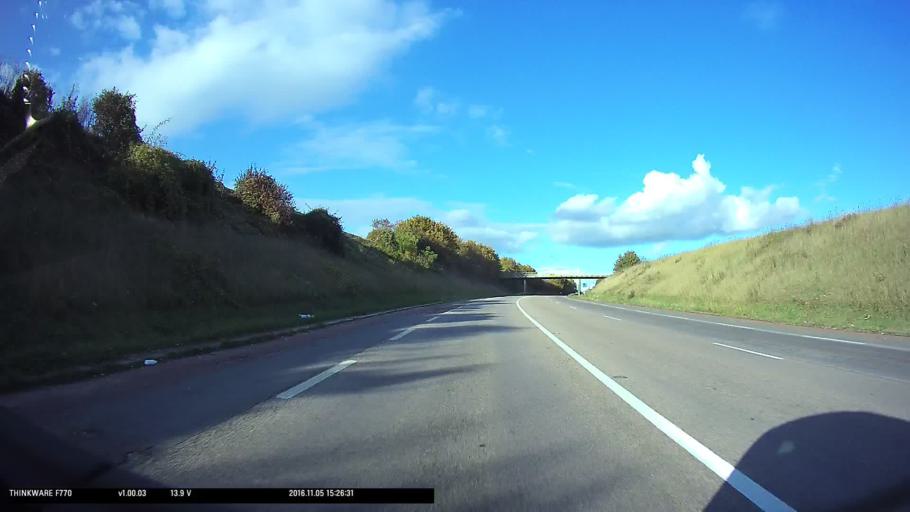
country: FR
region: Ile-de-France
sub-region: Departement des Yvelines
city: Meulan-en-Yvelines
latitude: 49.0231
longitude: 1.9098
